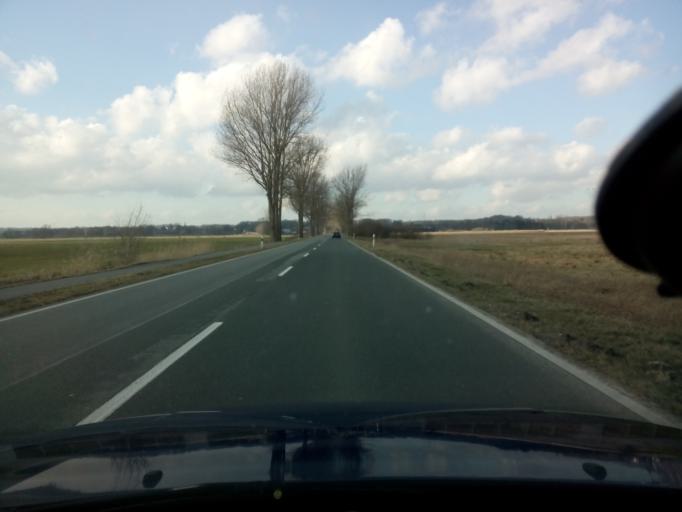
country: DE
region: Lower Saxony
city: Osterholz-Scharmbeck
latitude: 53.2116
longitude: 8.8174
